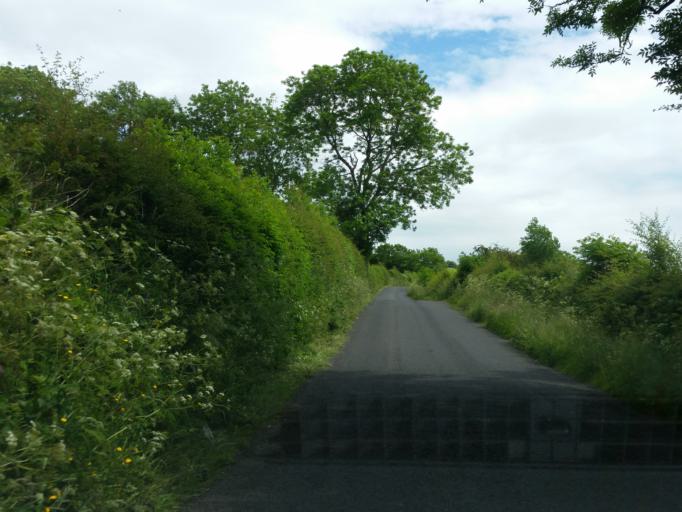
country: GB
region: Northern Ireland
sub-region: Omagh District
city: Omagh
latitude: 54.5485
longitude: -7.0891
